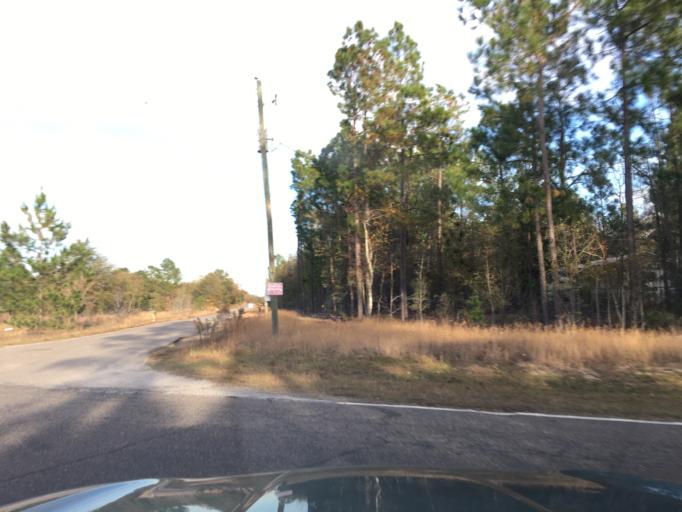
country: US
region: South Carolina
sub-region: Lexington County
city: Leesville
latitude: 33.6856
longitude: -81.3653
